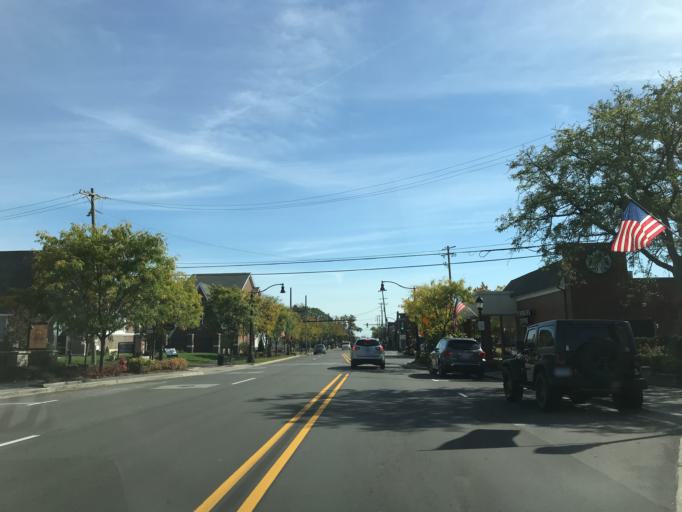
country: US
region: Michigan
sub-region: Oakland County
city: Farmington
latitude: 42.4642
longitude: -83.3747
